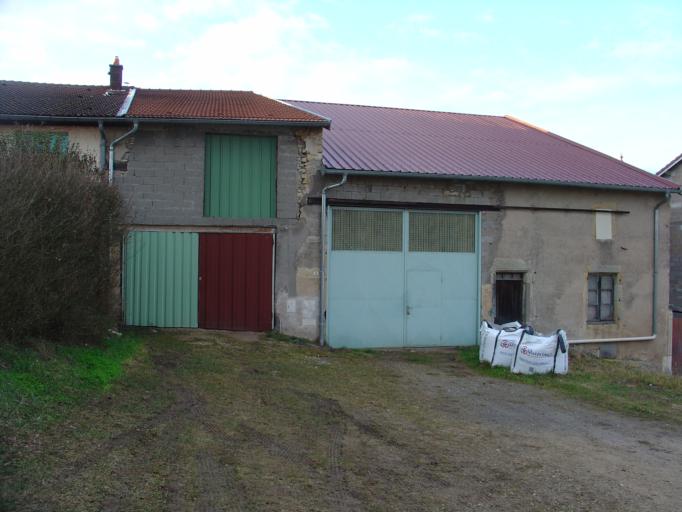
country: FR
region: Lorraine
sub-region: Departement de Meurthe-et-Moselle
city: Villey-Saint-Etienne
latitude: 48.7577
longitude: 5.9701
